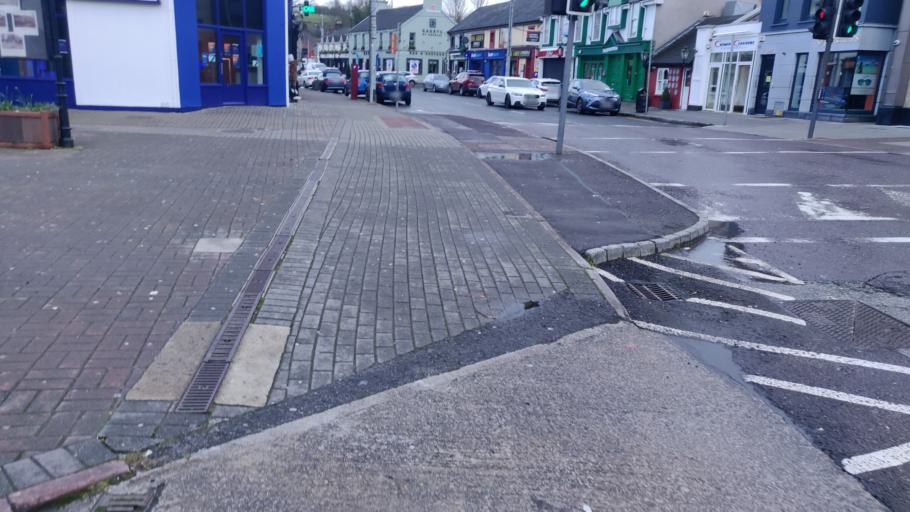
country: IE
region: Munster
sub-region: County Cork
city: Cork
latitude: 51.8780
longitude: -8.4365
